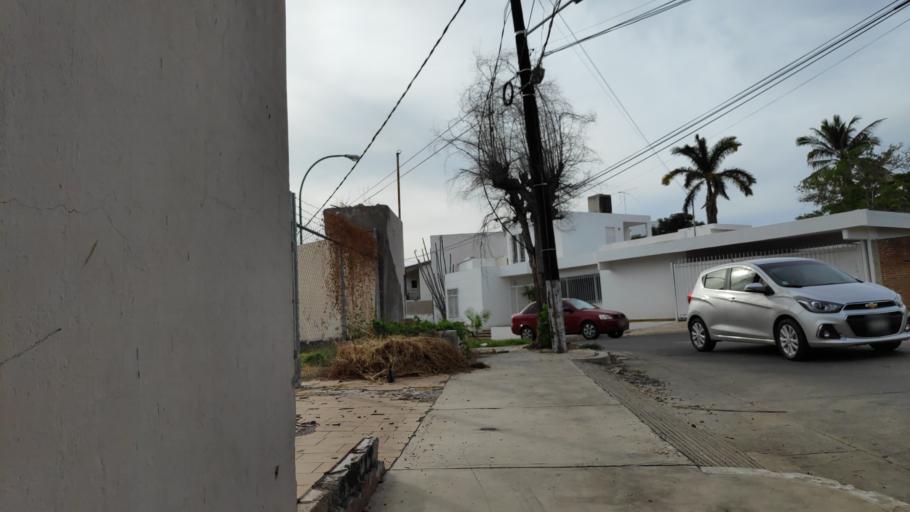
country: MX
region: Sinaloa
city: Culiacan
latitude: 24.7942
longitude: -107.3959
